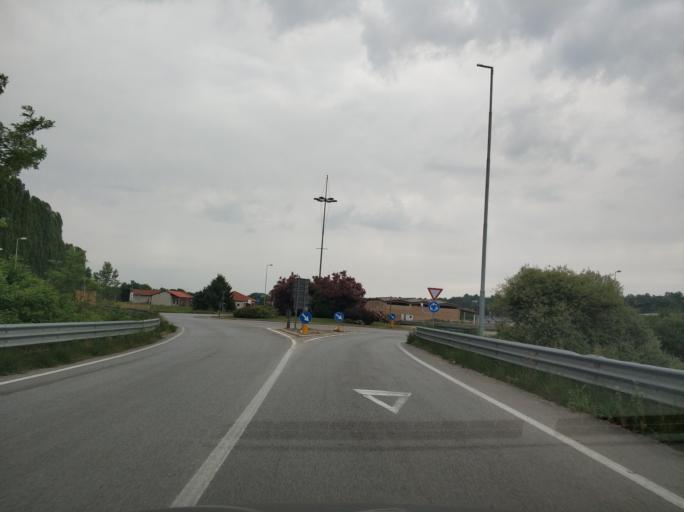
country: IT
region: Piedmont
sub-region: Provincia di Cuneo
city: Monta
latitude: 44.8236
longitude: 7.9441
